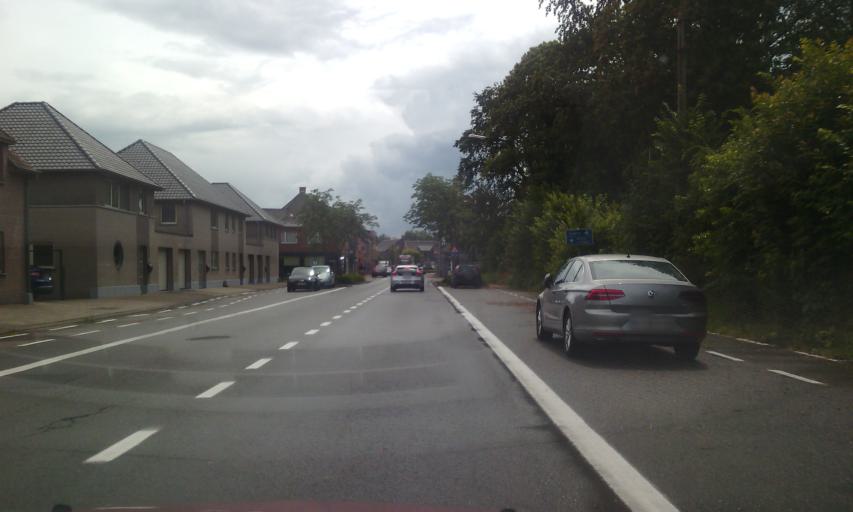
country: BE
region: Flanders
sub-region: Provincie Oost-Vlaanderen
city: Wetteren
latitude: 51.0138
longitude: 3.8809
